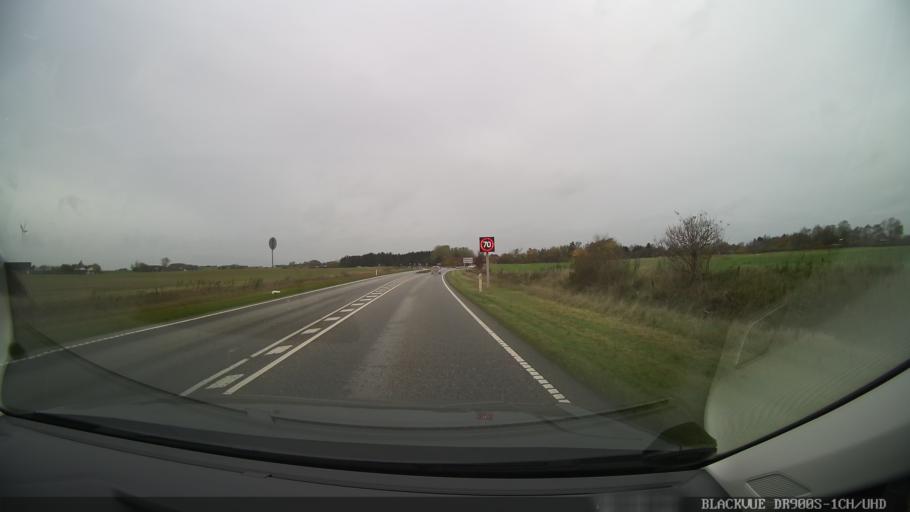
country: DK
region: North Denmark
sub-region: Thisted Kommune
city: Thisted
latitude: 56.8288
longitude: 8.7159
